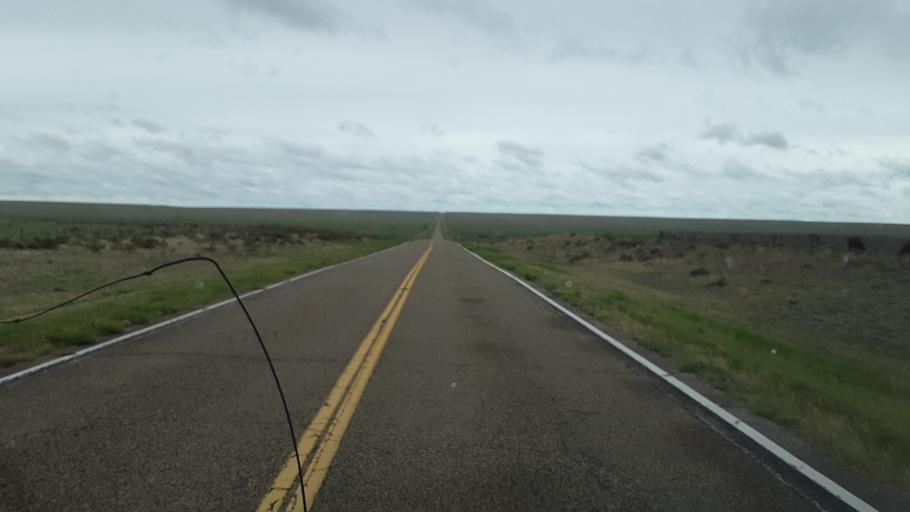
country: US
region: Colorado
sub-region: Lincoln County
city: Hugo
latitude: 38.8499
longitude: -103.3580
